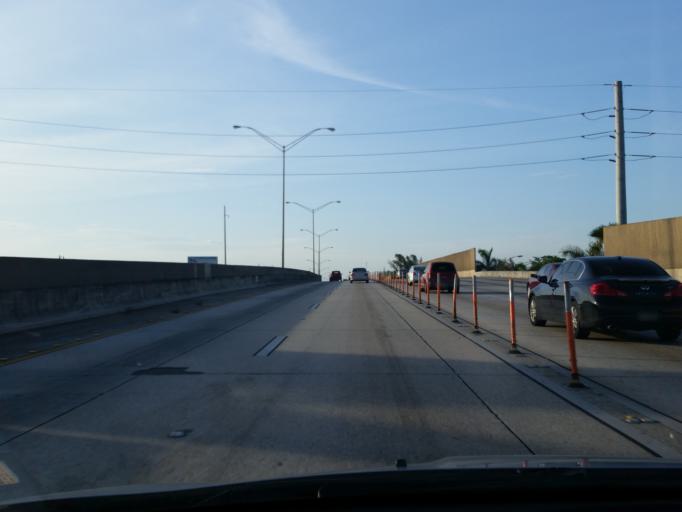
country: US
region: Florida
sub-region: Miami-Dade County
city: Golden Glades
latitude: 25.8976
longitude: -80.2096
